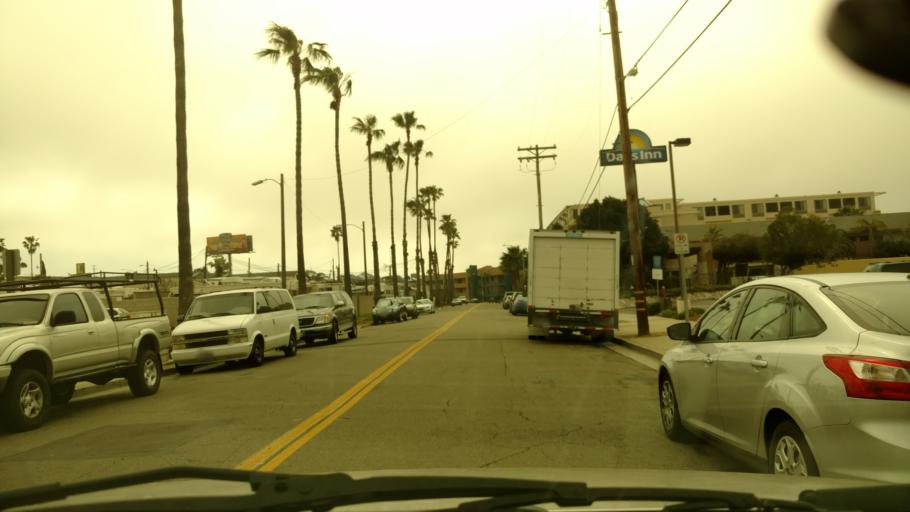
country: US
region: California
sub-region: San Diego County
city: Oceanside
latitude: 33.2085
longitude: -117.3885
